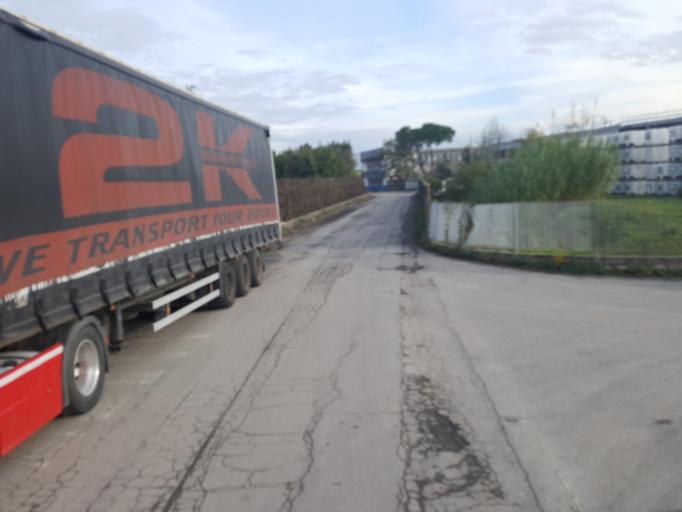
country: IT
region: Tuscany
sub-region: Provincia di Lucca
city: Porcari
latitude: 43.8225
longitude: 10.6135
